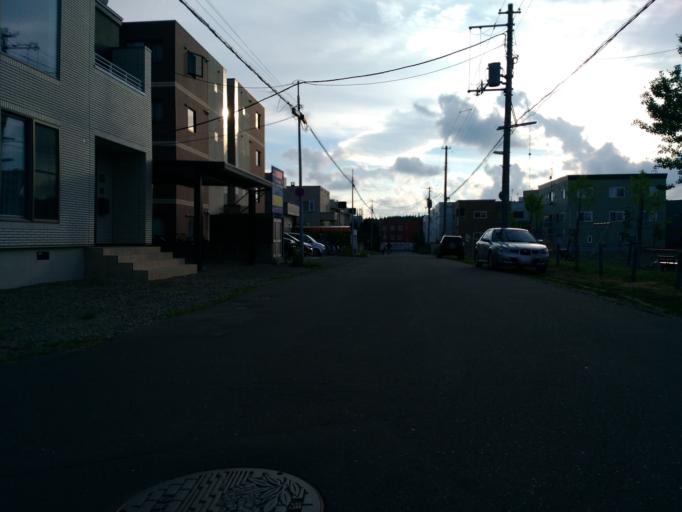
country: JP
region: Hokkaido
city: Ebetsu
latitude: 43.0690
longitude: 141.4956
